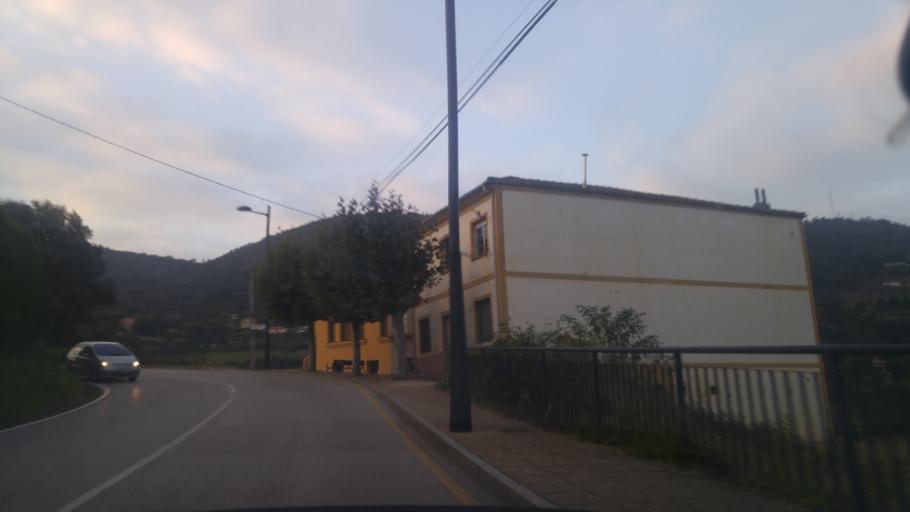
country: ES
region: Asturias
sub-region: Province of Asturias
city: Oviedo
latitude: 43.3738
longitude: -5.8624
